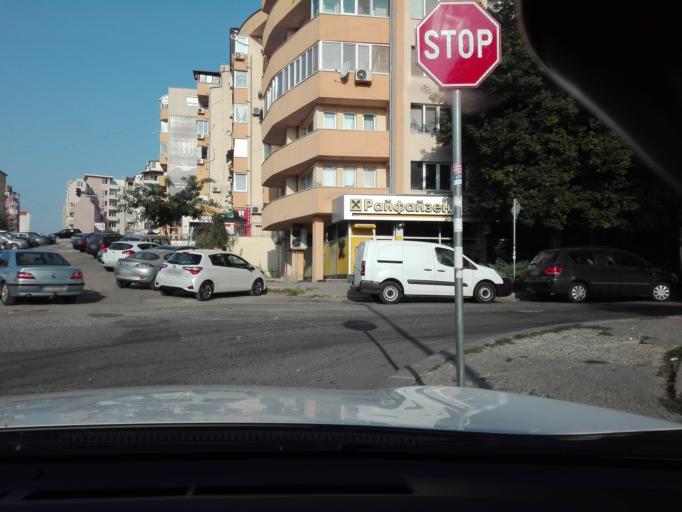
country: BG
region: Burgas
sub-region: Obshtina Burgas
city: Burgas
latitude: 42.4615
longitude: 27.4151
